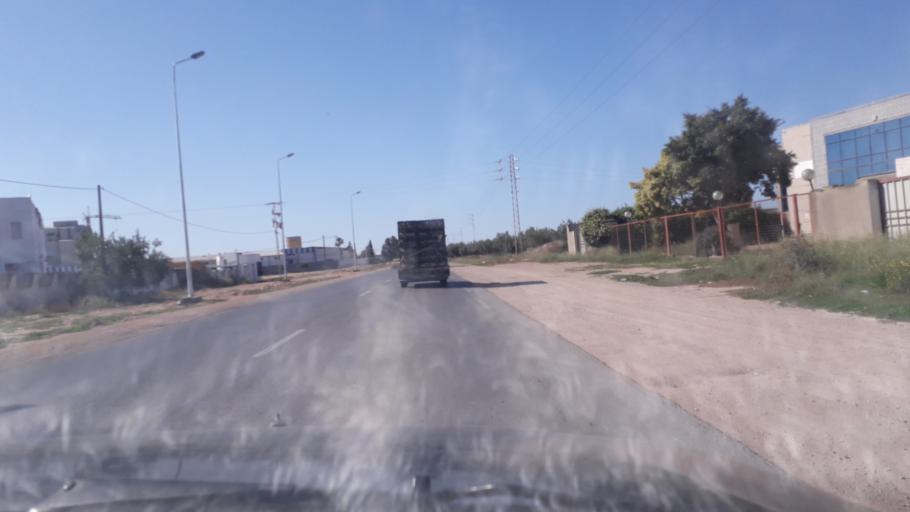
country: TN
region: Safaqis
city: Al Qarmadah
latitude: 34.8648
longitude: 10.7580
